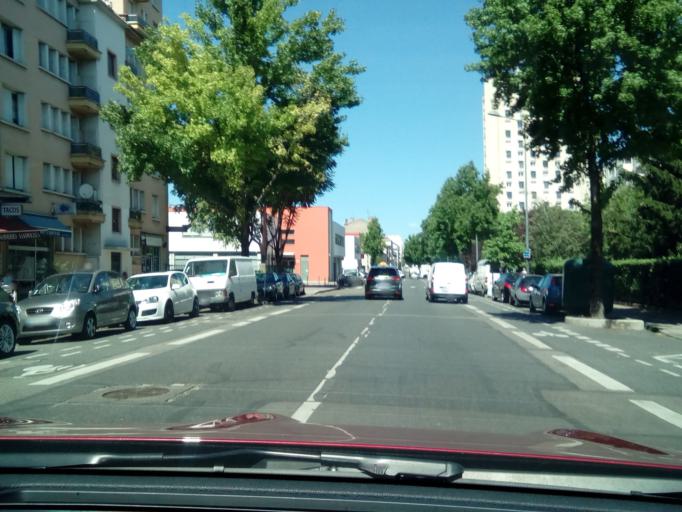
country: FR
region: Rhone-Alpes
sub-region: Departement du Rhone
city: Villeurbanne
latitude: 45.7632
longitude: 4.8846
